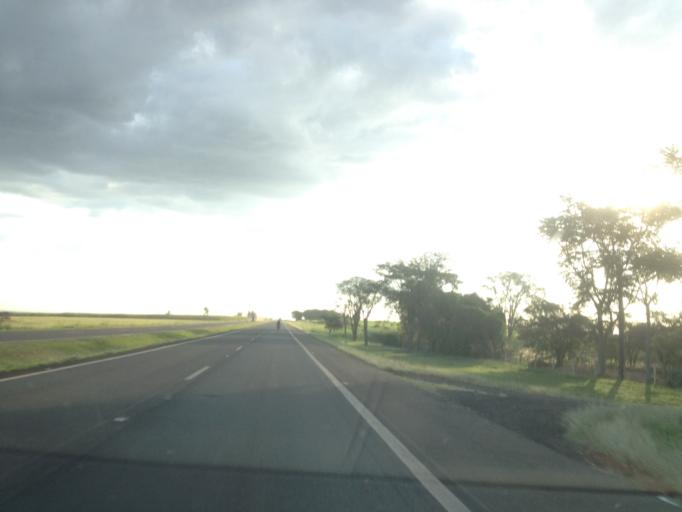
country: BR
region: Sao Paulo
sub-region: Jau
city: Jau
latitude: -22.2691
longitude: -48.4606
